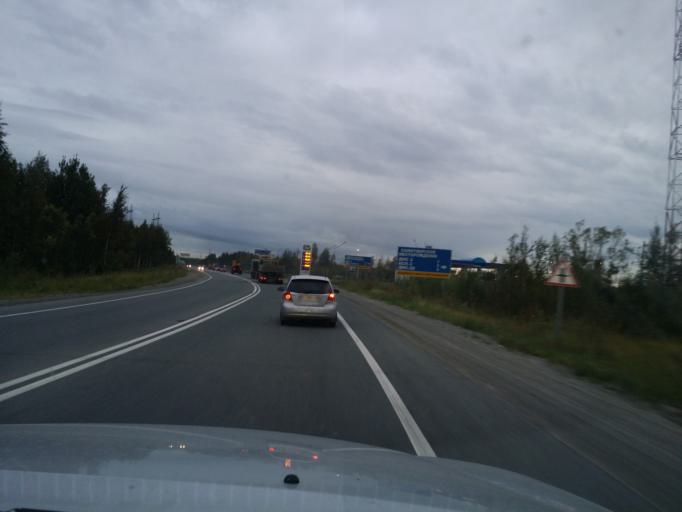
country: RU
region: Khanty-Mansiyskiy Avtonomnyy Okrug
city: Izluchinsk
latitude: 61.0136
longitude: 76.7772
